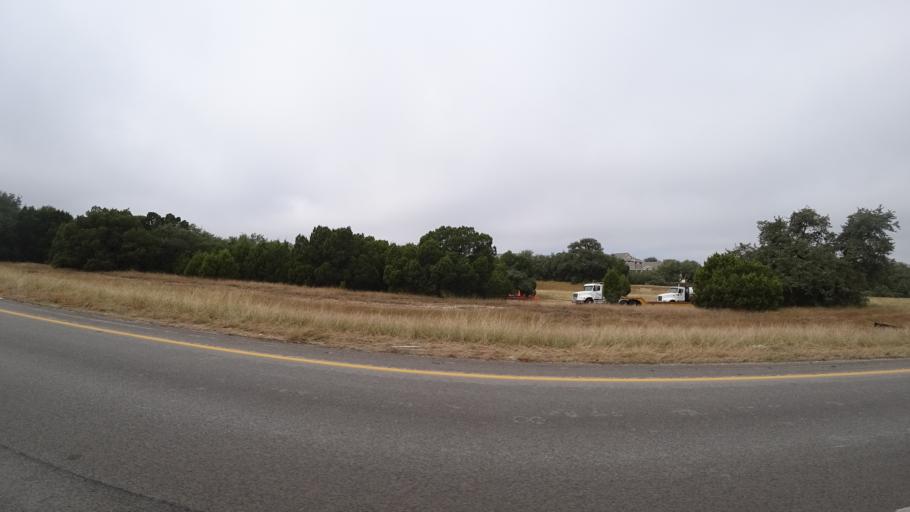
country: US
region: Texas
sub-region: Travis County
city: Shady Hollow
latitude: 30.2032
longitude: -97.8641
